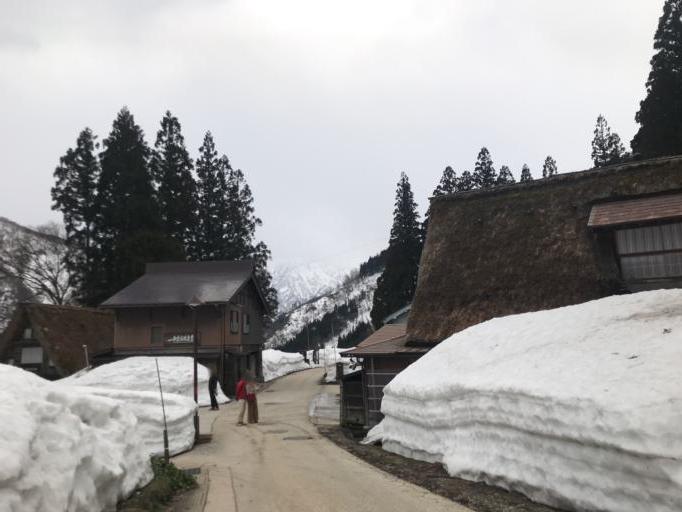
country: JP
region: Toyama
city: Nanto-shi
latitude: 36.4250
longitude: 136.9349
